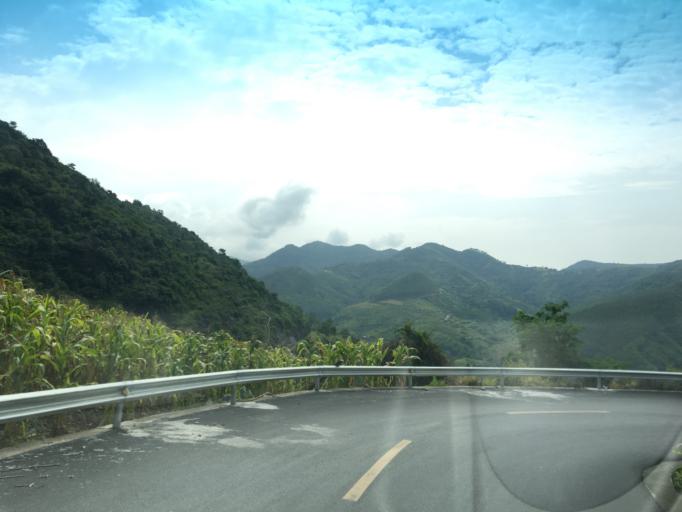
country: CN
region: Guangxi Zhuangzu Zizhiqu
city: Xinzhou
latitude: 24.8225
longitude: 105.6479
